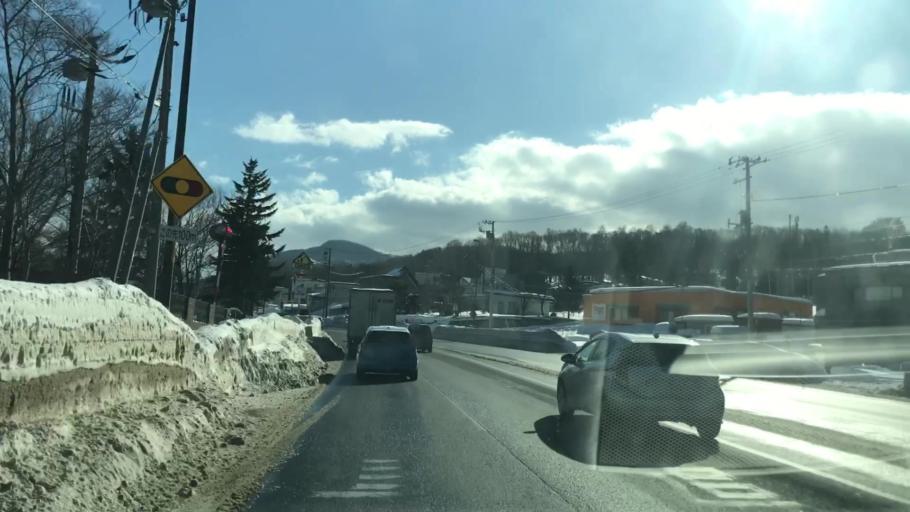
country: JP
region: Hokkaido
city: Otaru
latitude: 43.1505
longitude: 141.1328
